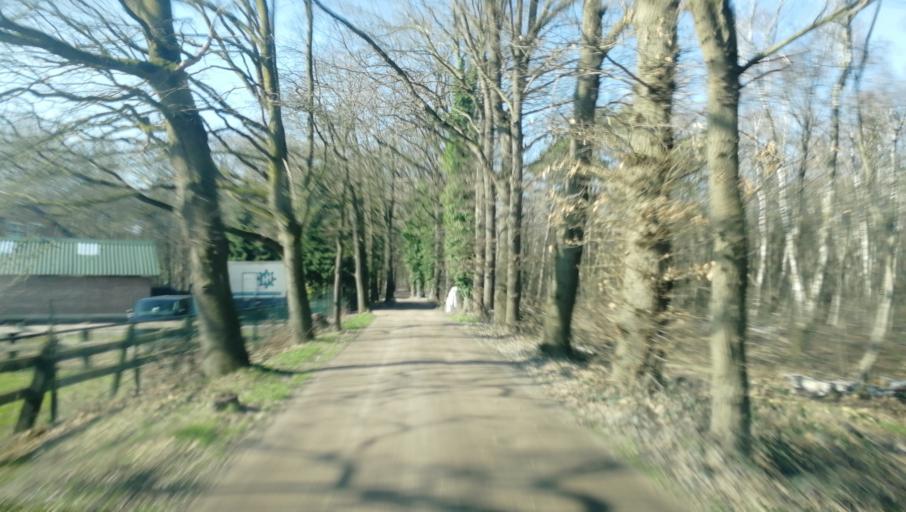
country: NL
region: Limburg
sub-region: Gemeente Venlo
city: Venlo
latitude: 51.3949
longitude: 6.1929
